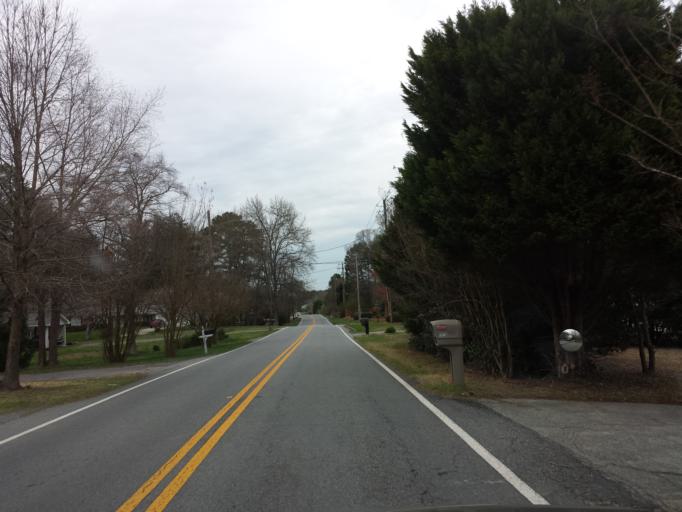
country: US
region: Georgia
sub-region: Cobb County
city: Marietta
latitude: 34.0081
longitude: -84.5112
